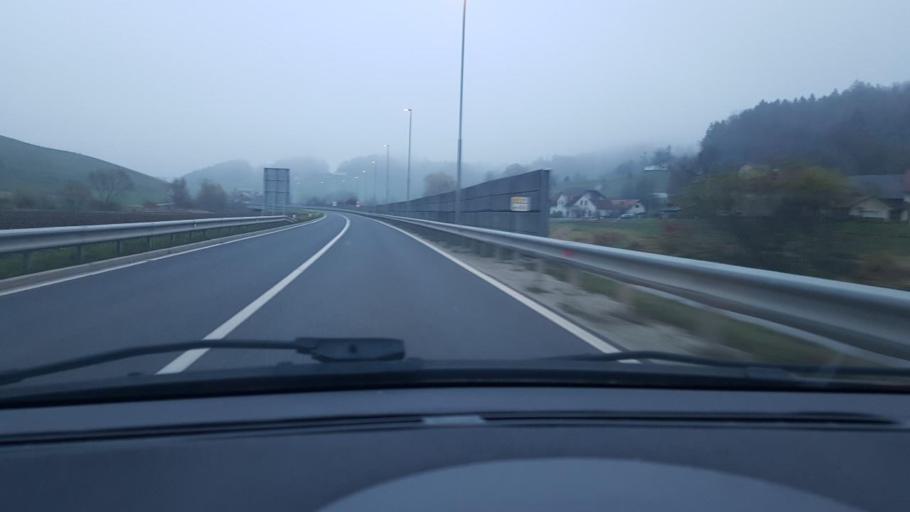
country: SI
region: Sentjur pri Celju
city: Sentjur
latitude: 46.2148
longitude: 15.4464
